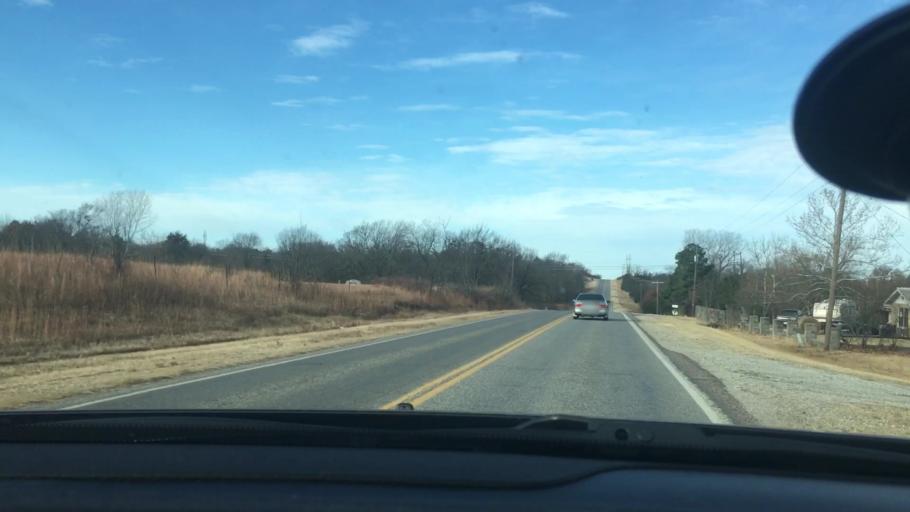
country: US
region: Oklahoma
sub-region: Seminole County
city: Konawa
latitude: 34.9458
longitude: -96.7280
